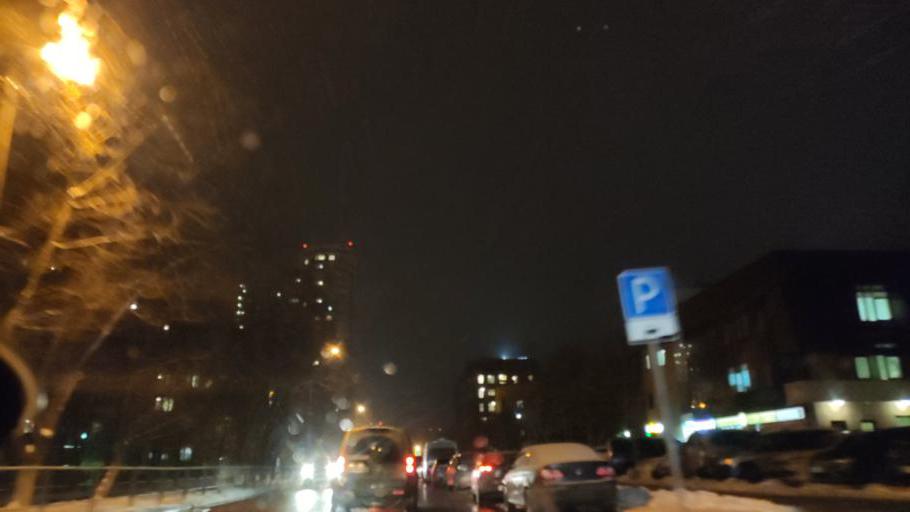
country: RU
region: Moskovskaya
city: Odintsovo
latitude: 55.6849
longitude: 37.2625
